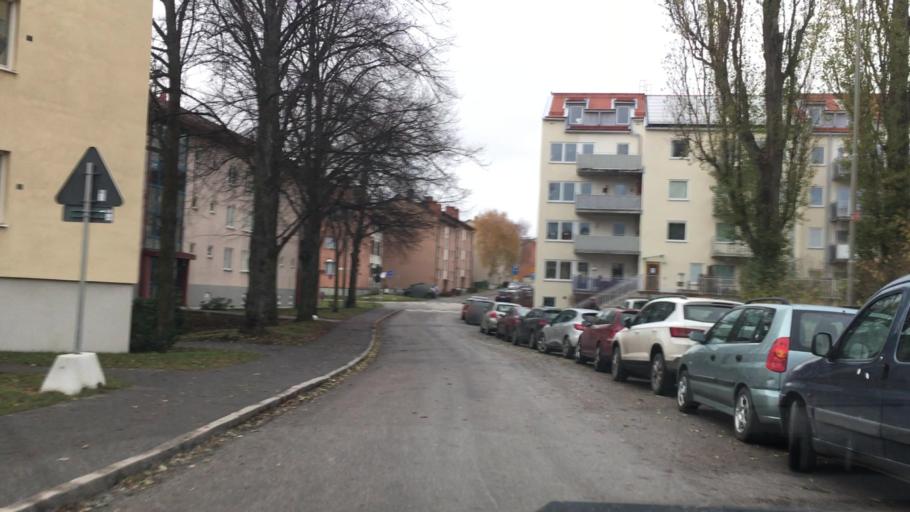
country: SE
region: Stockholm
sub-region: Stockholms Kommun
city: Arsta
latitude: 59.2975
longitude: 18.0463
